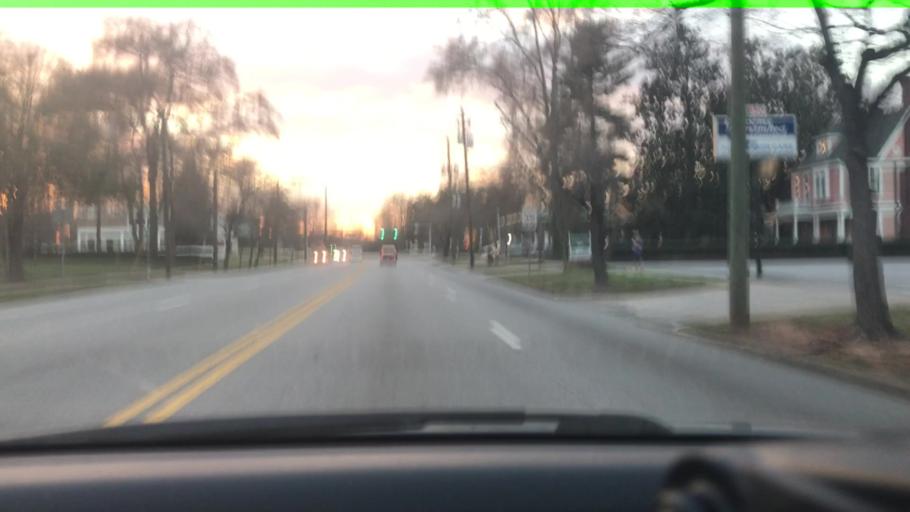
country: US
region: Georgia
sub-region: Clarke County
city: Athens
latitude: 33.9618
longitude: -83.3915
